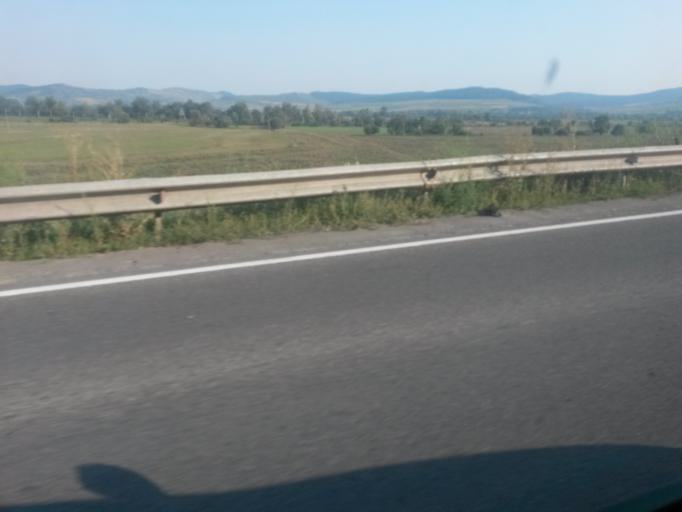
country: RO
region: Alba
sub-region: Comuna Unirea
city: Unirea
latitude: 46.3922
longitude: 23.7905
